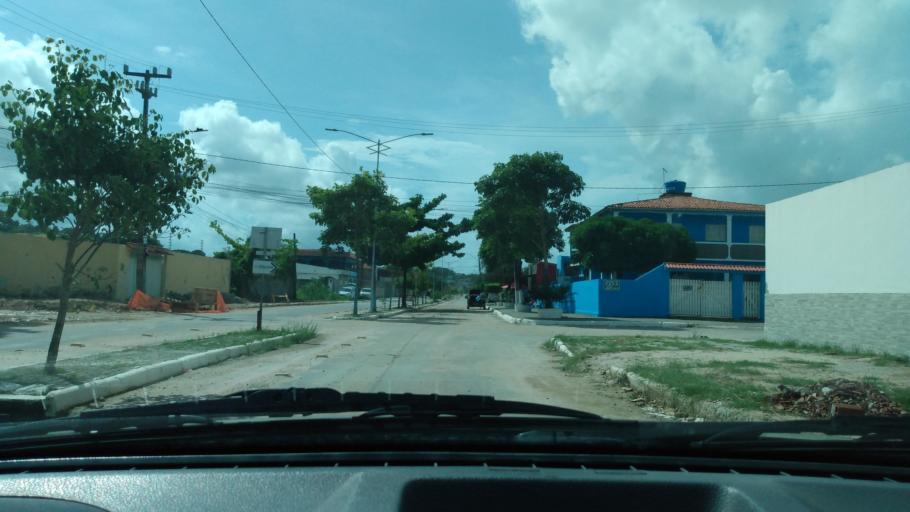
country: BR
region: Pernambuco
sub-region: Cabo De Santo Agostinho
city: Cabo
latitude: -8.3281
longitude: -34.9536
